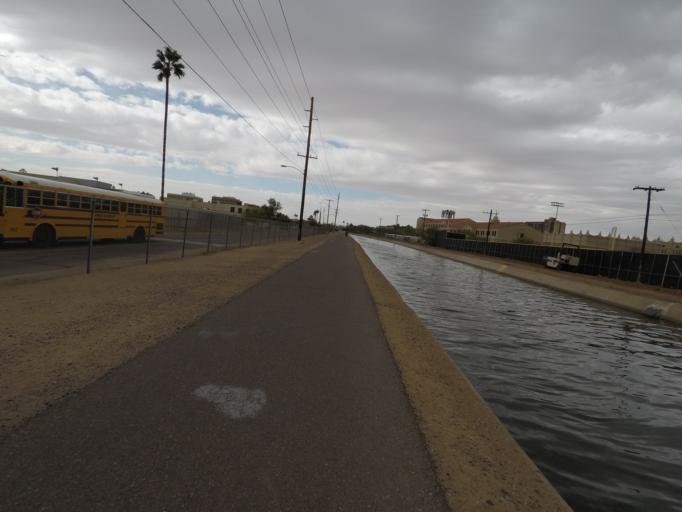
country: US
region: Arizona
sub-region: Maricopa County
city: Phoenix
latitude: 33.5034
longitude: -112.0694
